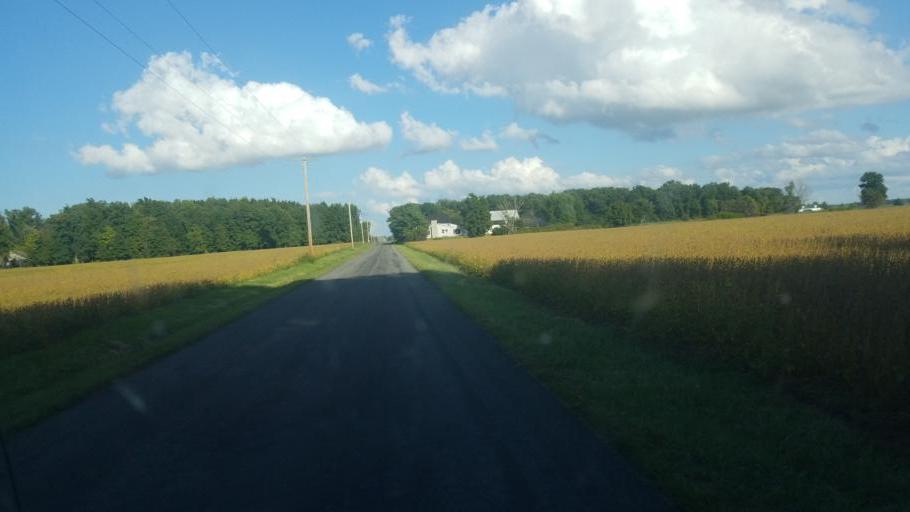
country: US
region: Ohio
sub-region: Hancock County
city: Arlington
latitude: 40.9362
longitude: -83.7175
